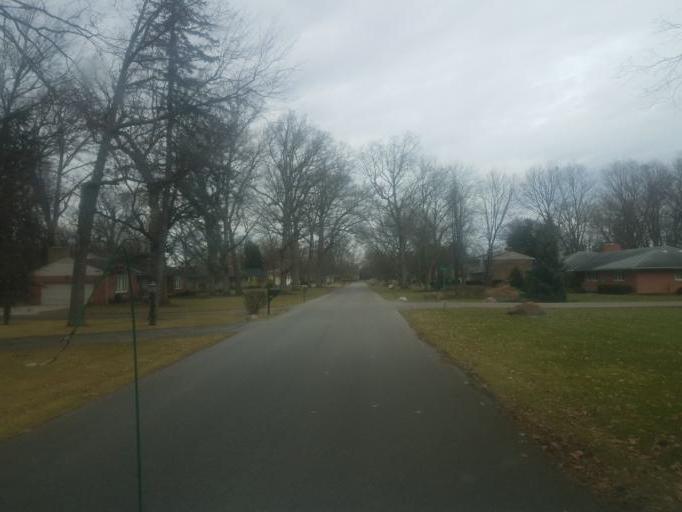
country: US
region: Ohio
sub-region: Marion County
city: Marion
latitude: 40.5674
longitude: -83.0827
